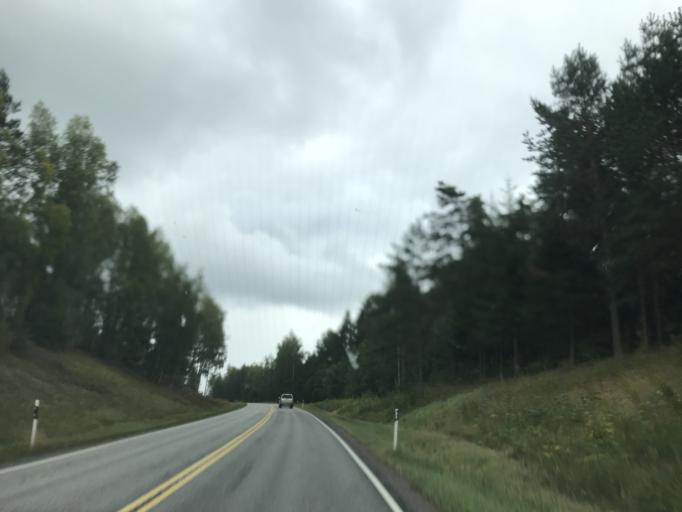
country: FI
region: Varsinais-Suomi
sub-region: Salo
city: Pernioe
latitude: 60.0823
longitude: 23.2366
